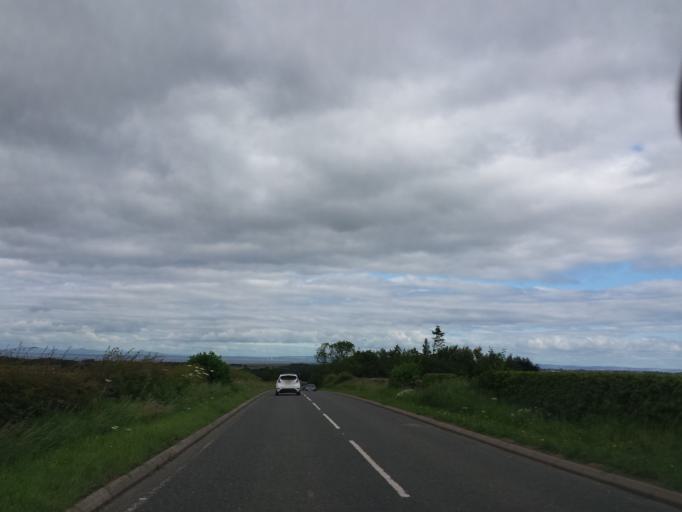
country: GB
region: Scotland
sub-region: East Lothian
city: Haddington
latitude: 55.9842
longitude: -2.8248
